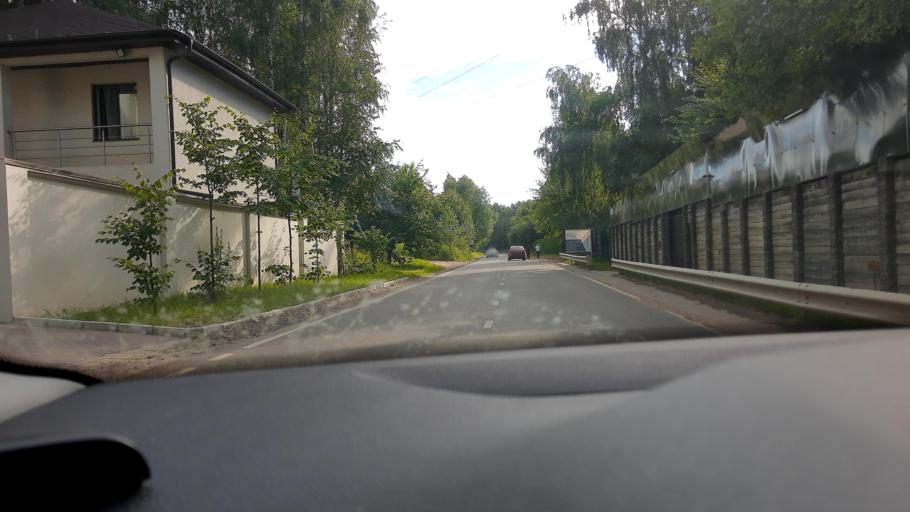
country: RU
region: Moscow
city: Severnyy
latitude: 55.9710
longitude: 37.5429
